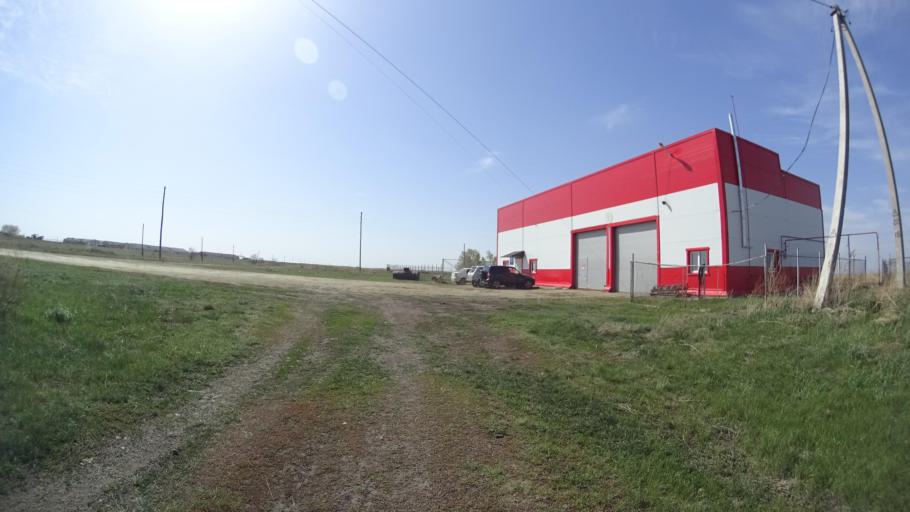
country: RU
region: Chelyabinsk
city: Chesma
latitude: 53.7875
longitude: 61.0393
